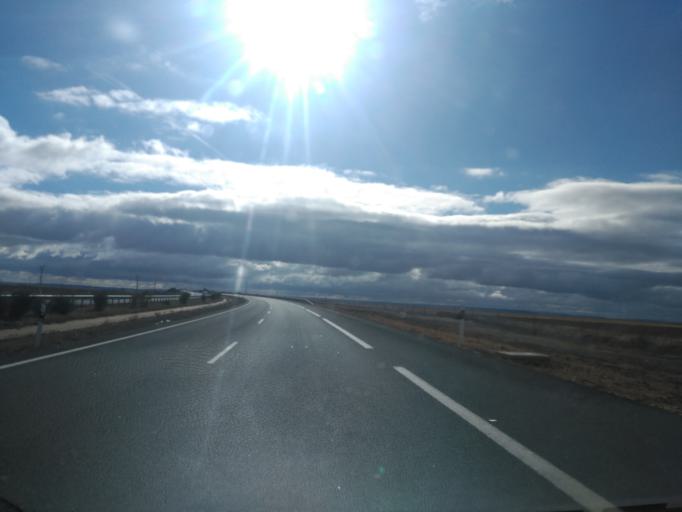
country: ES
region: Castille and Leon
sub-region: Provincia de Palencia
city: Marcilla de Campos
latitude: 42.3150
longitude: -4.4028
